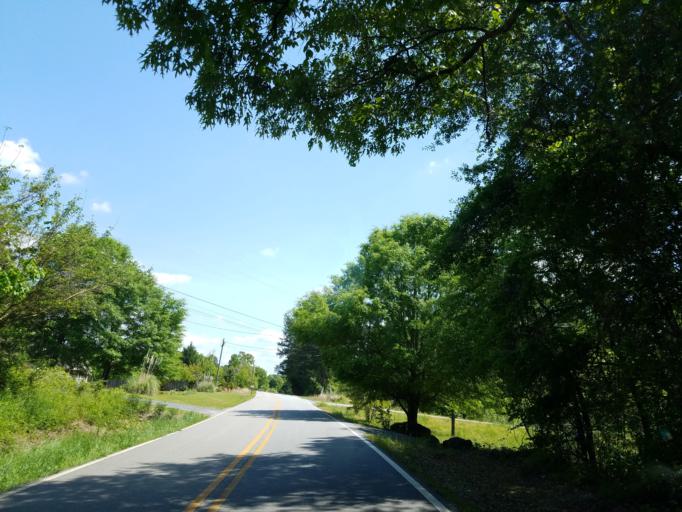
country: US
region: Georgia
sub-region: Butts County
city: Indian Springs
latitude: 33.1745
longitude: -84.0247
